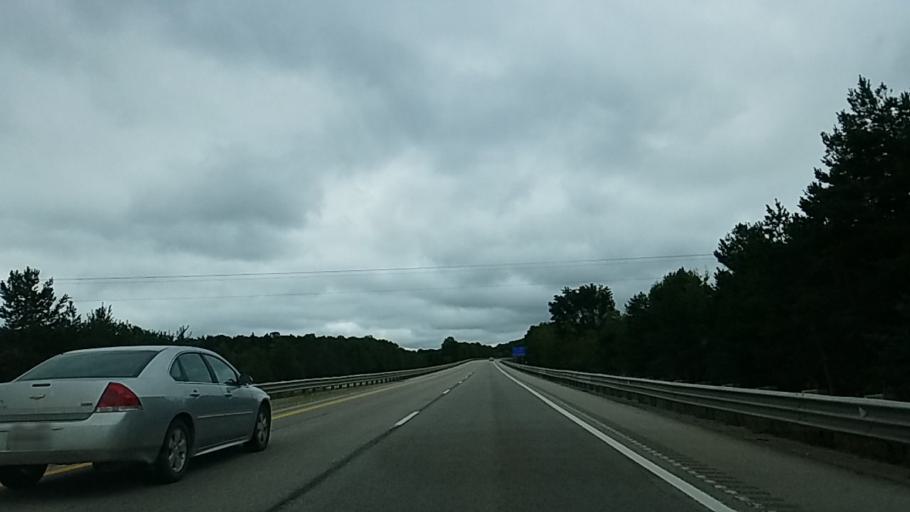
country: US
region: Michigan
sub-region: Otsego County
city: Gaylord
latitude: 45.1292
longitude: -84.6719
